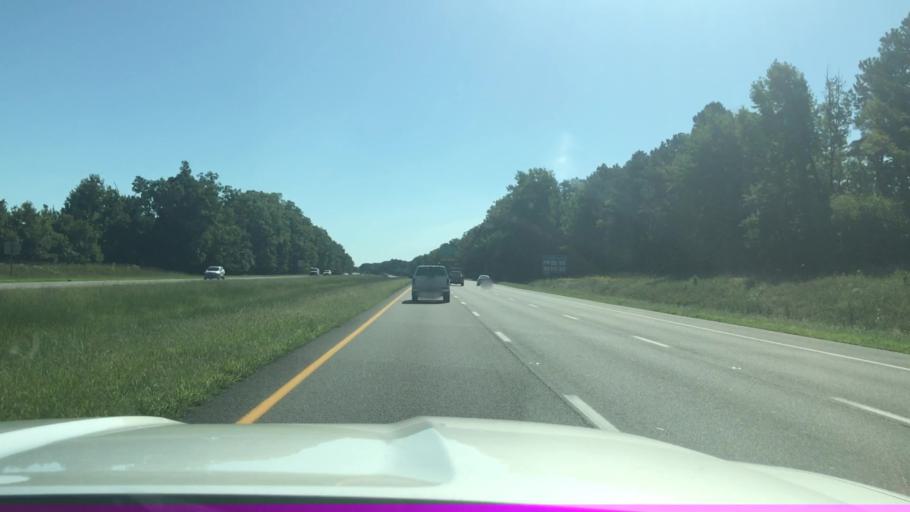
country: US
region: Virginia
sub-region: Henrico County
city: Highland Springs
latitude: 37.5309
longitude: -77.3412
